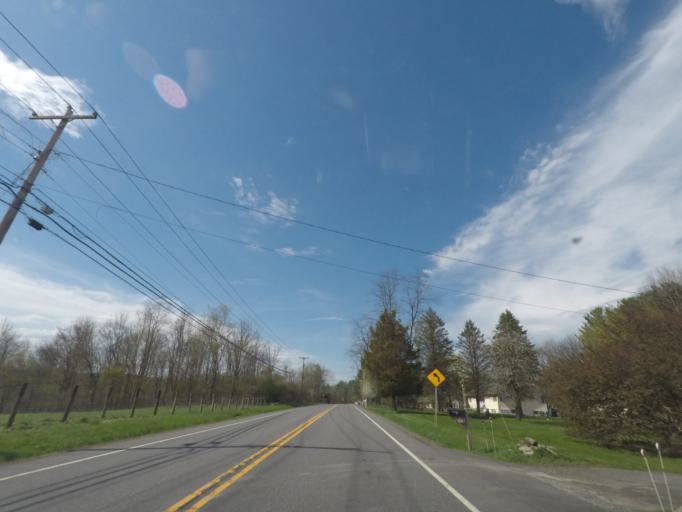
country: US
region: New York
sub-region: Greene County
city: Cairo
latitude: 42.3270
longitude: -74.0151
